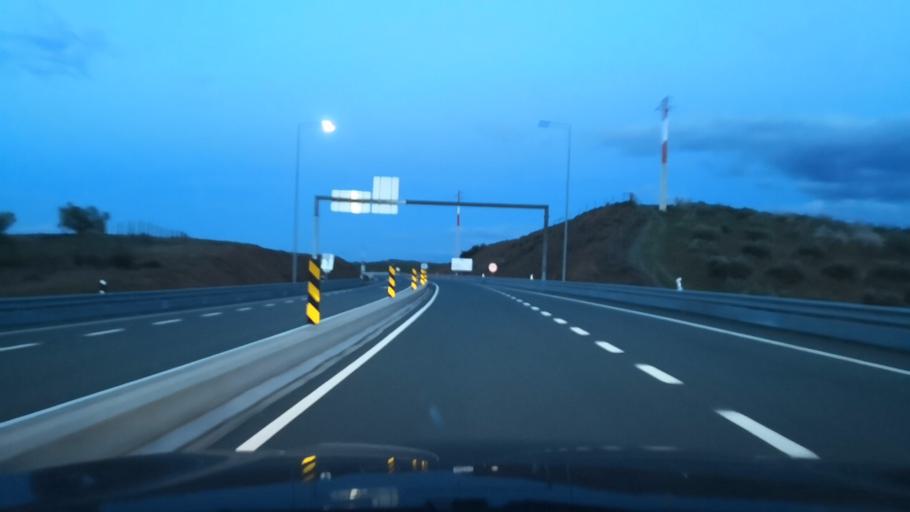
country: PT
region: Braganca
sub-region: Alfandega da Fe
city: Alfandega da Fe
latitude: 41.3244
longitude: -6.9768
